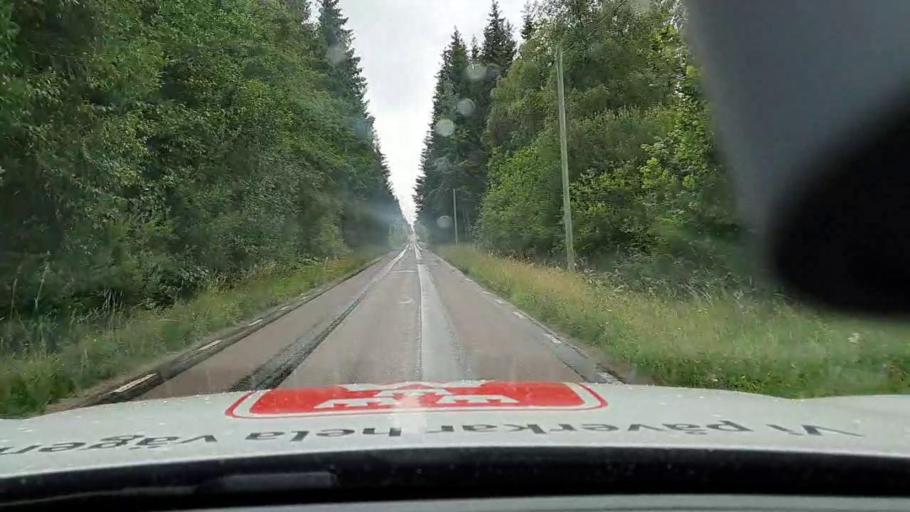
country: SE
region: Vaestra Goetaland
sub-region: Skovde Kommun
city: Skoevde
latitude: 58.4469
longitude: 13.7624
